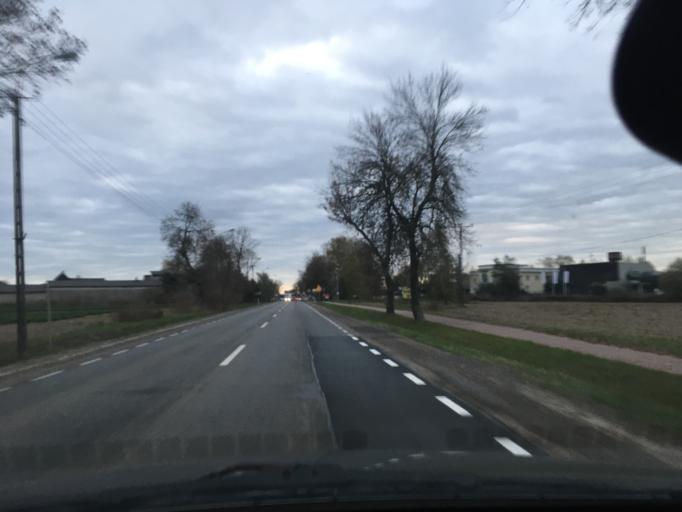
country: PL
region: Masovian Voivodeship
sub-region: Powiat piaseczynski
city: Lesznowola
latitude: 52.0928
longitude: 20.9301
